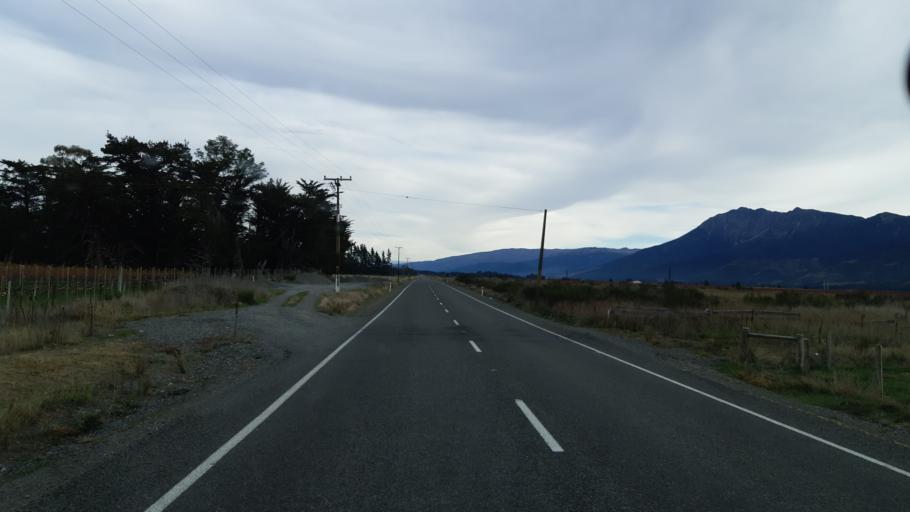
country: NZ
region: Tasman
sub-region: Tasman District
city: Richmond
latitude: -41.6174
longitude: 173.3758
